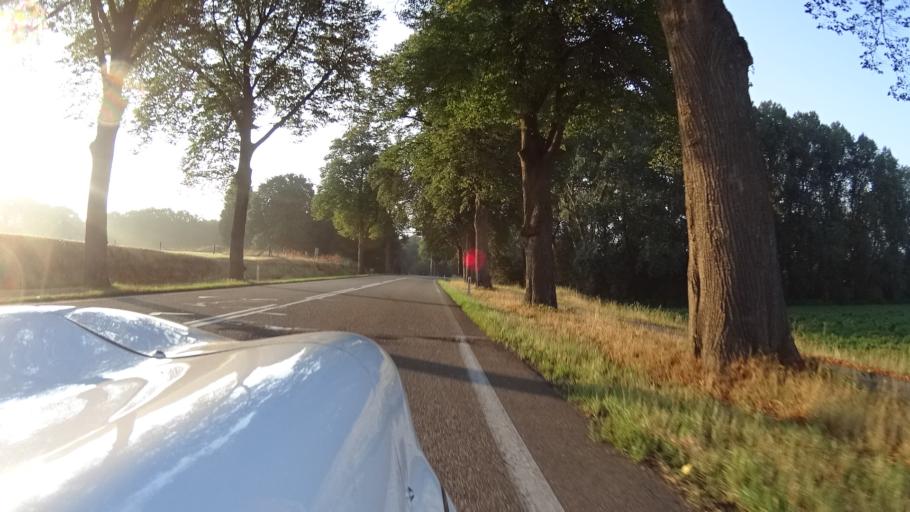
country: NL
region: Limburg
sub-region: Gemeente Bergen
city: Wellerlooi
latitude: 51.5501
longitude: 6.1126
